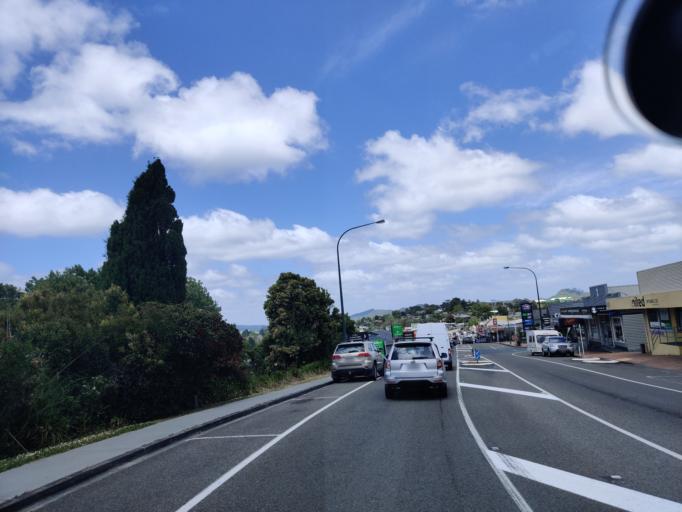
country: NZ
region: Auckland
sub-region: Auckland
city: Wellsford
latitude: -36.2925
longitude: 174.5244
